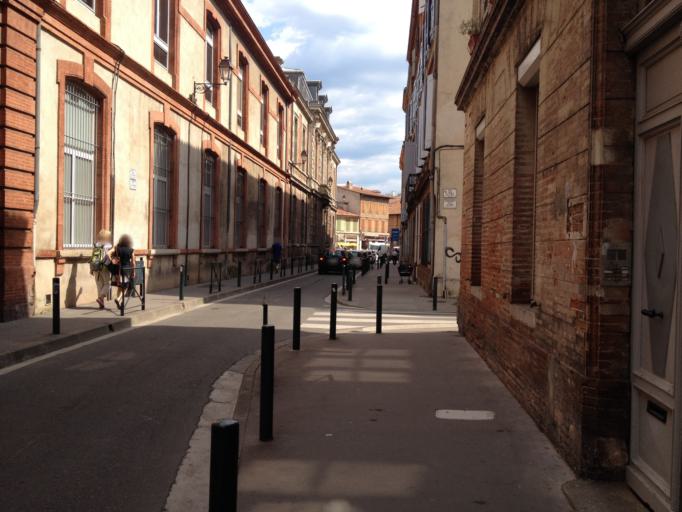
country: FR
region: Midi-Pyrenees
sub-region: Departement de la Haute-Garonne
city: Toulouse
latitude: 43.6068
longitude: 1.4390
